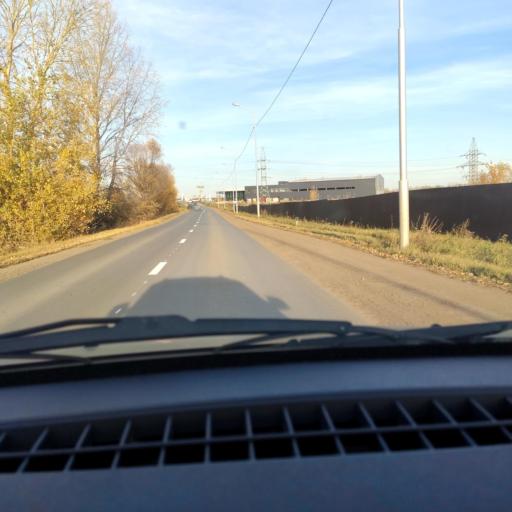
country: RU
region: Bashkortostan
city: Ufa
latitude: 54.6676
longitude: 55.9217
